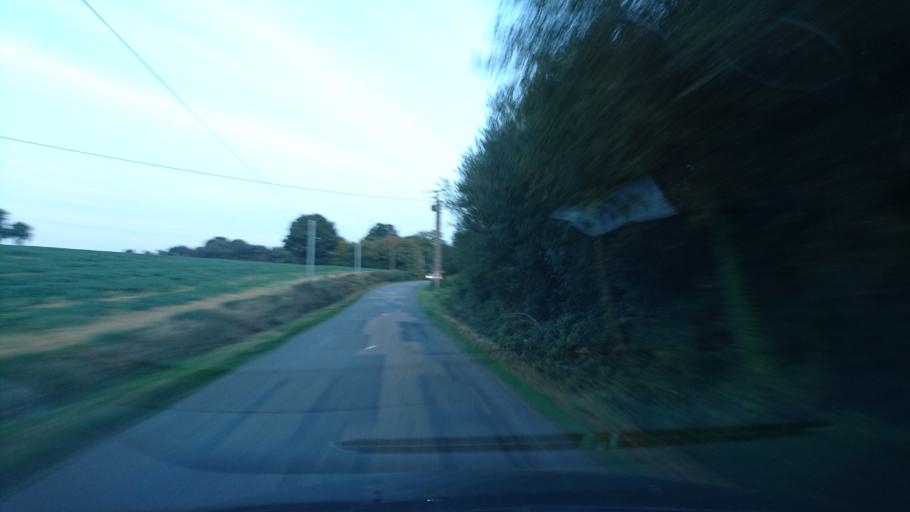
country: FR
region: Brittany
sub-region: Departement d'Ille-et-Vilaine
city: Guignen
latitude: 47.9074
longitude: -1.9200
